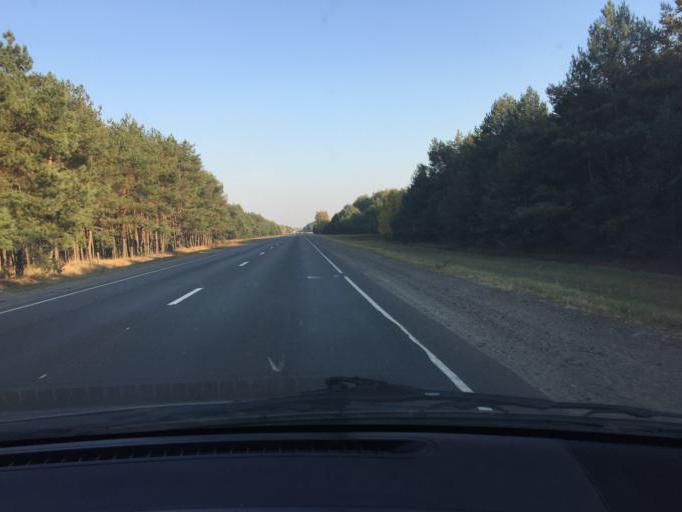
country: BY
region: Brest
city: Davyd-Haradok
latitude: 52.2393
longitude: 27.2111
